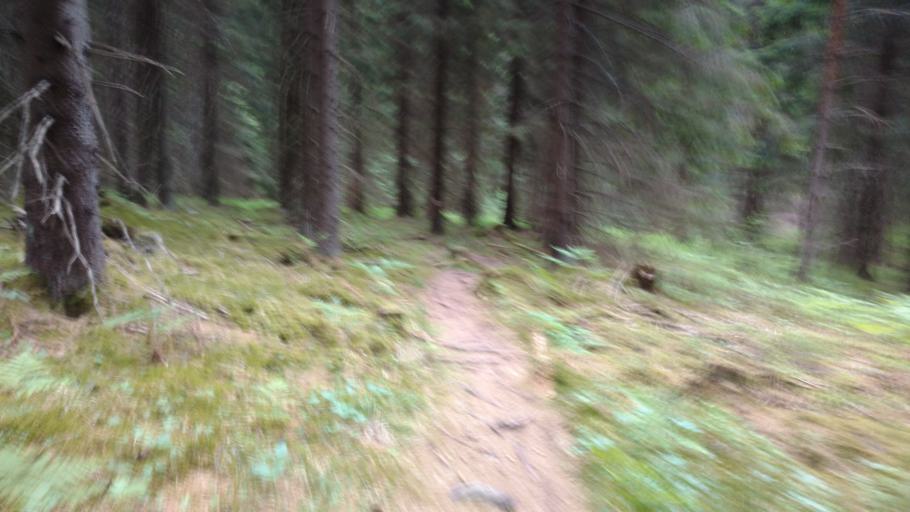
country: FI
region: Uusimaa
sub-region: Raaseporin
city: Pohja
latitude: 60.1182
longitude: 23.5600
